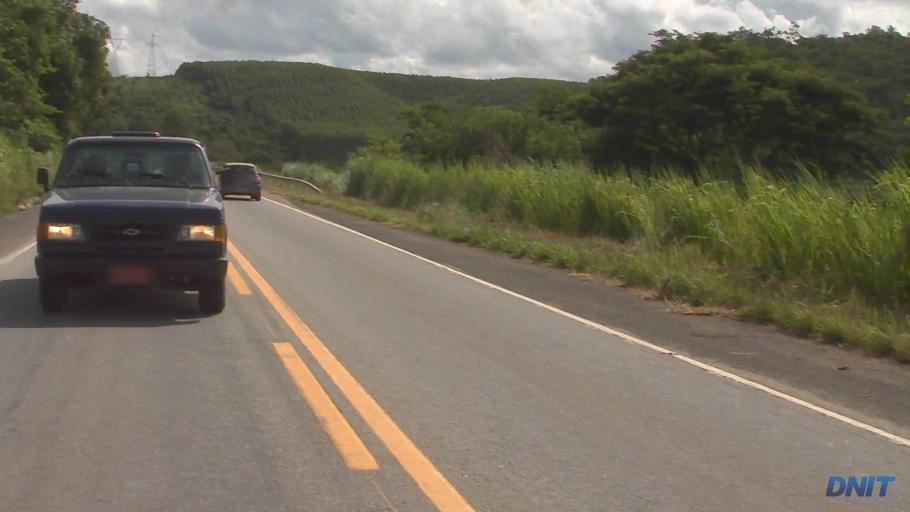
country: BR
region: Minas Gerais
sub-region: Ipaba
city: Ipaba
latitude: -19.3979
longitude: -42.4839
